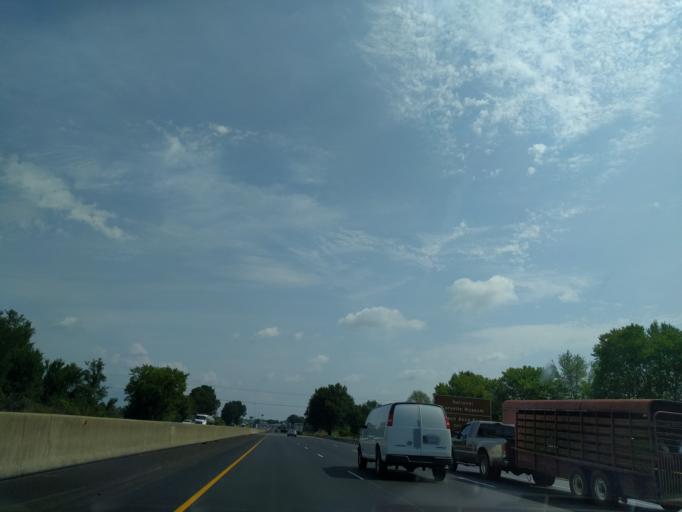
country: US
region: Kentucky
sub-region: Warren County
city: Bowling Green
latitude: 36.9970
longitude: -86.3786
